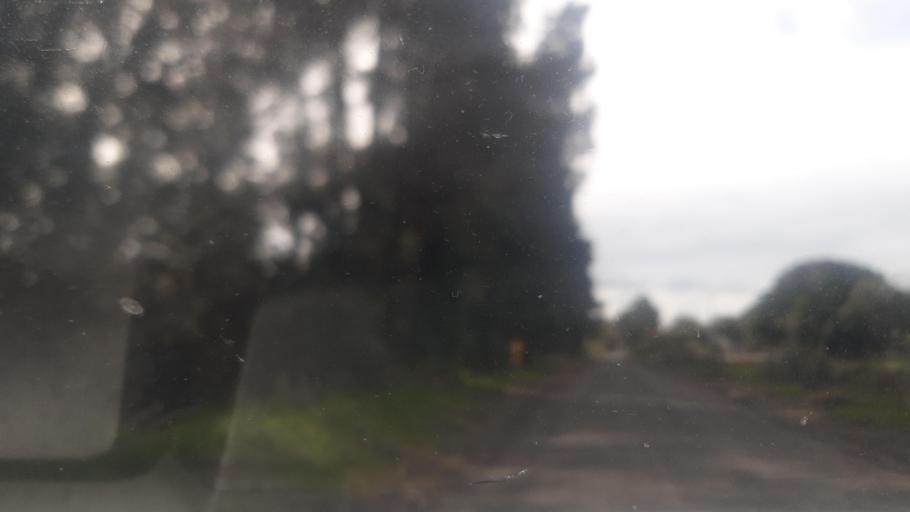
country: NZ
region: Northland
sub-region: Far North District
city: Kaitaia
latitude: -35.0397
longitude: 173.2235
